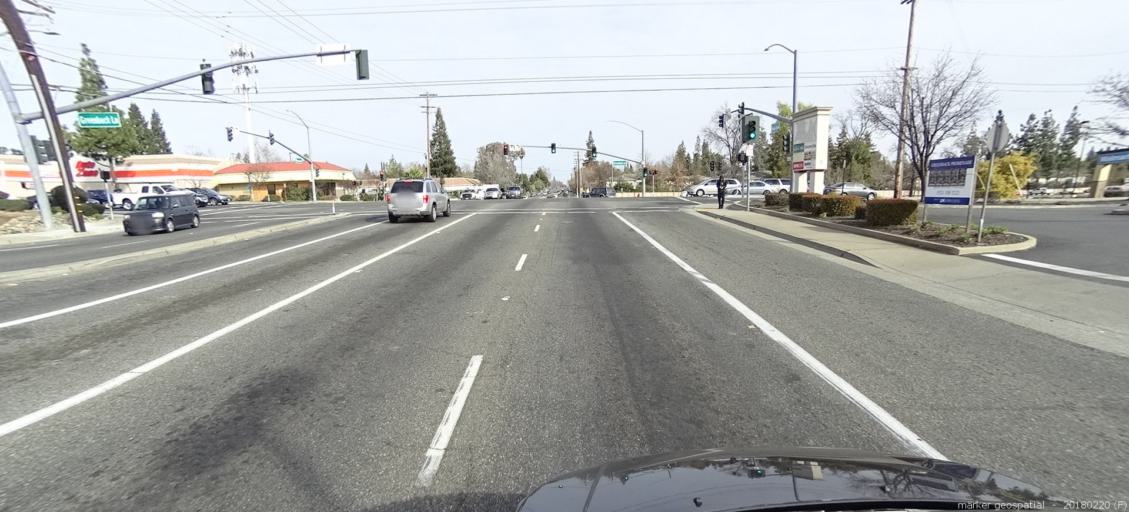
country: US
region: California
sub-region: Sacramento County
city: Orangevale
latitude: 38.6780
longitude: -121.2256
